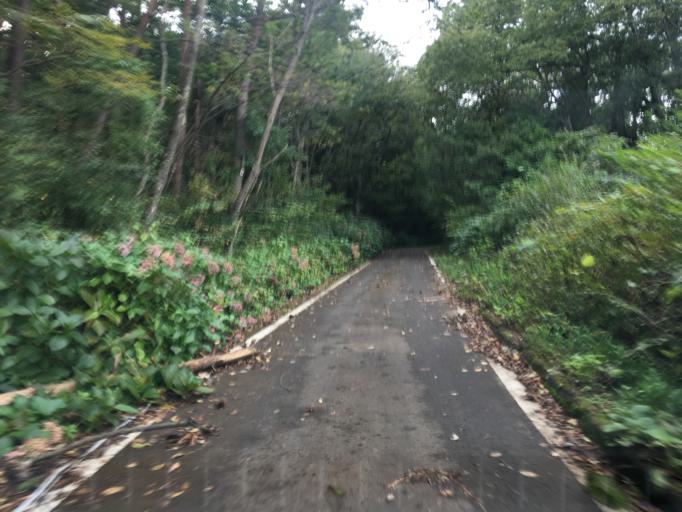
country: JP
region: Miyagi
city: Marumori
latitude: 37.9203
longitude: 140.7175
